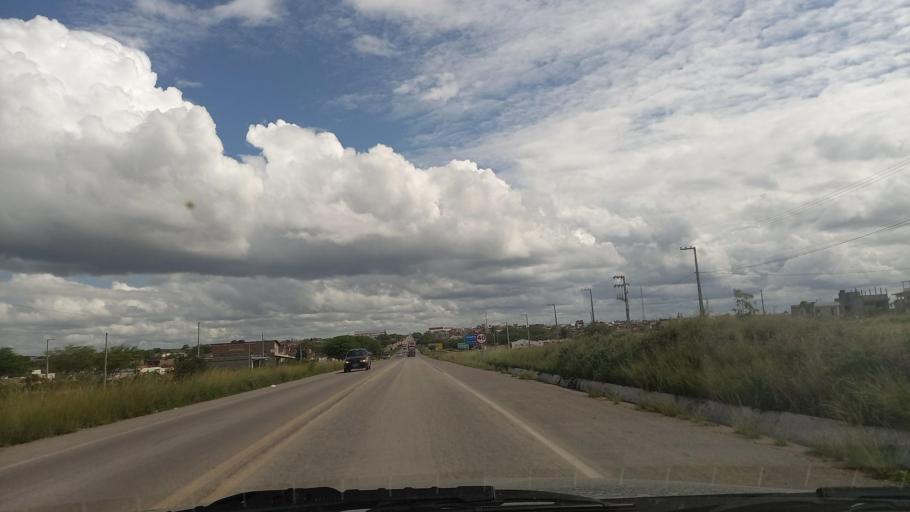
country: BR
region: Pernambuco
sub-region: Cachoeirinha
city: Cachoeirinha
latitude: -8.4850
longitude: -36.2271
